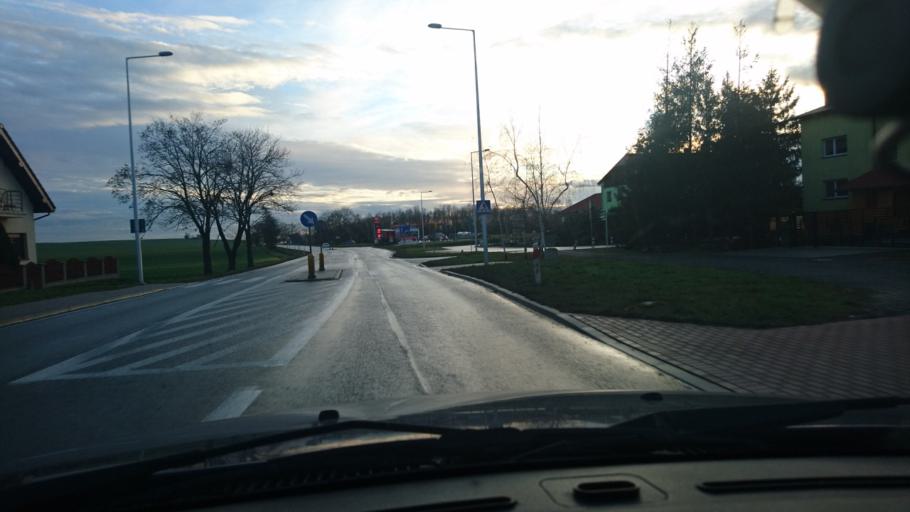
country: PL
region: Opole Voivodeship
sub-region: Powiat kluczborski
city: Byczyna
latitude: 51.1097
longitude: 18.2073
